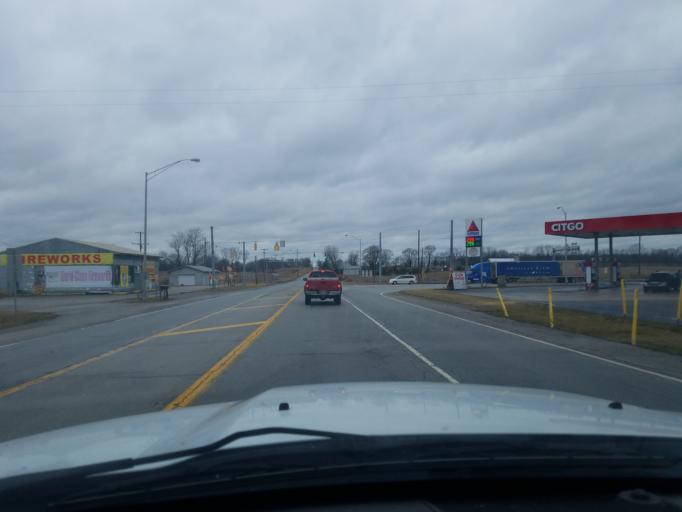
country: US
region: Indiana
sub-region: Noble County
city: Rome City
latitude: 41.4529
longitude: -85.3697
